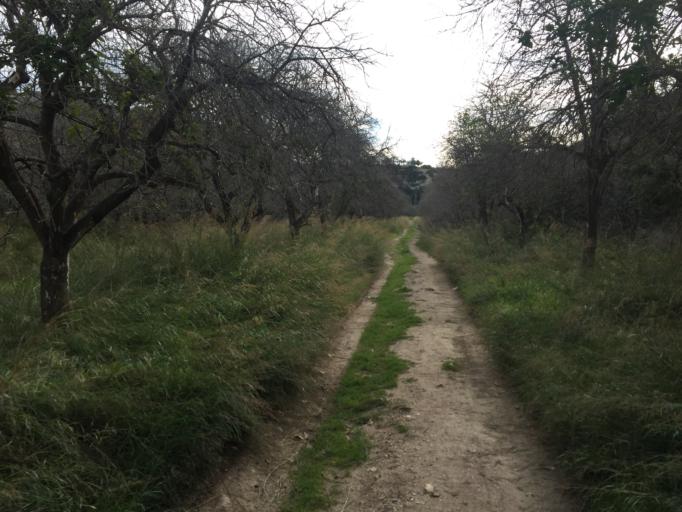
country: CY
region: Pafos
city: Pegeia
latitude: 34.9188
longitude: 32.3298
